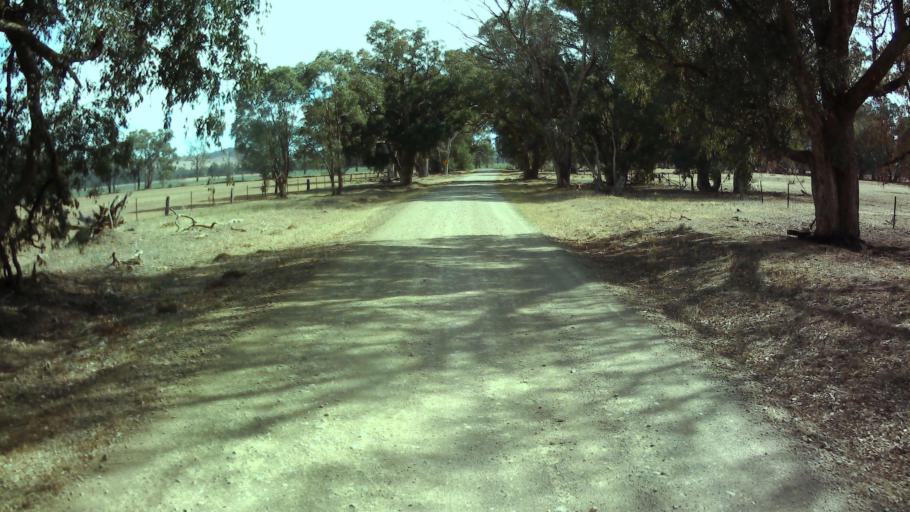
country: AU
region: New South Wales
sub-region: Weddin
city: Grenfell
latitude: -33.6892
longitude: 148.3046
